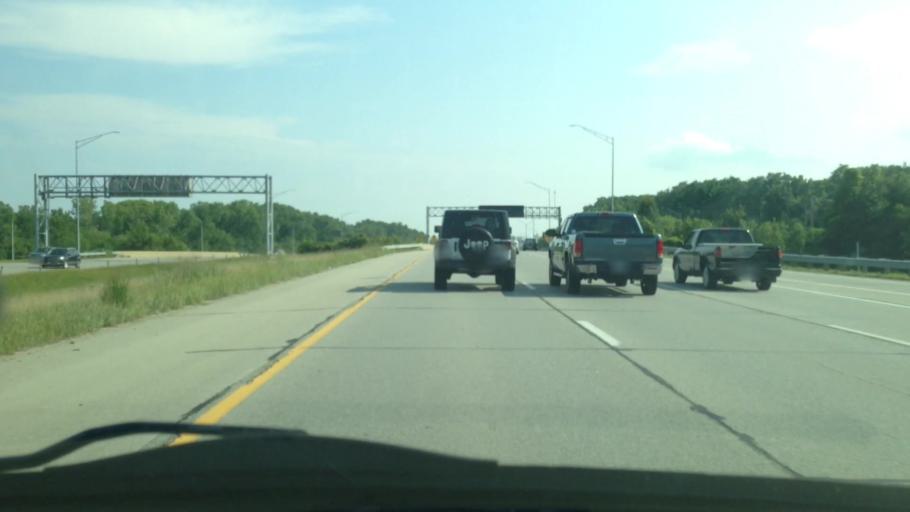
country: US
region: Iowa
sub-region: Linn County
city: Cedar Rapids
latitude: 42.0084
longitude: -91.6664
